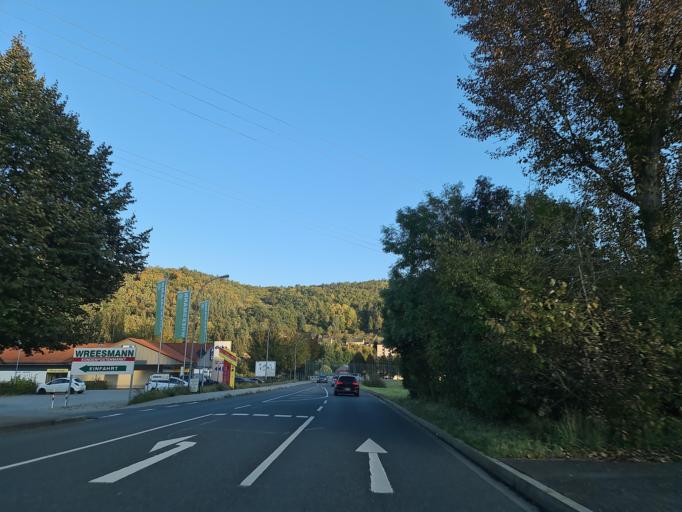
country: DE
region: Saxony
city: Elsterberg
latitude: 50.6113
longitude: 12.1724
